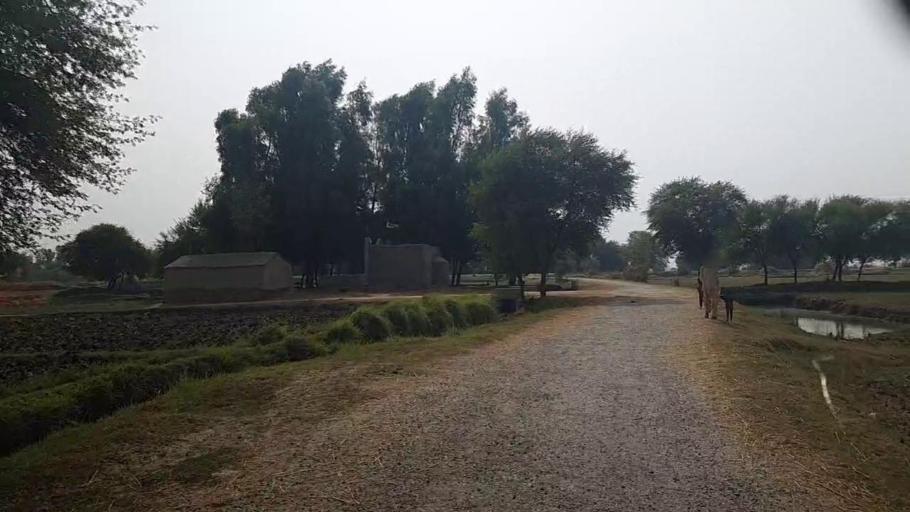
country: PK
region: Sindh
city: Kashmor
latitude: 28.3792
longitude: 69.4463
